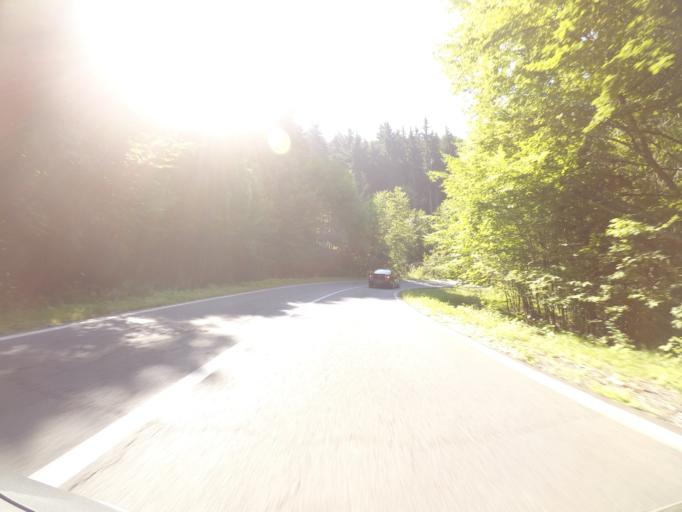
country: RO
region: Brasov
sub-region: Comuna Cristian
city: Cristian
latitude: 45.5829
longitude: 25.5113
